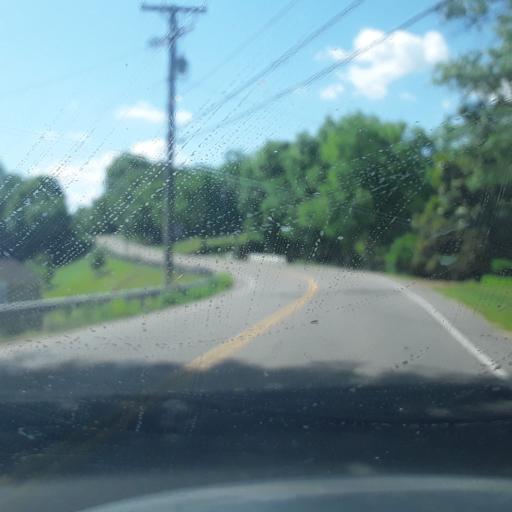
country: US
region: Tennessee
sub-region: Williamson County
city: Brentwood Estates
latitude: 36.0299
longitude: -86.6986
